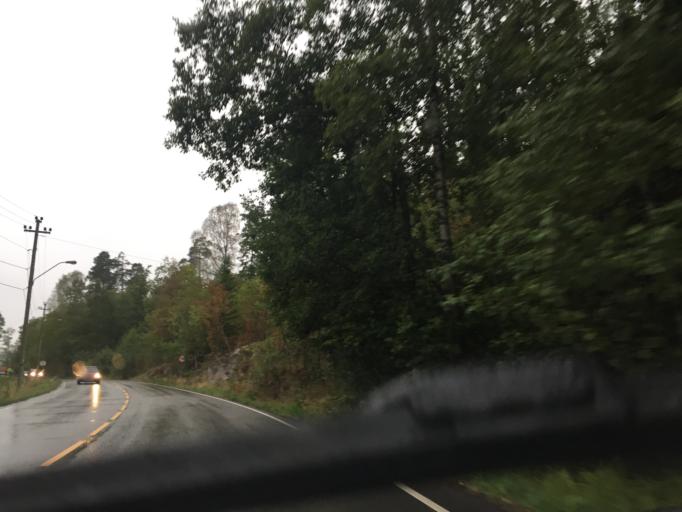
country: NO
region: Akershus
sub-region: Baerum
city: Lysaker
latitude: 59.9716
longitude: 10.6346
